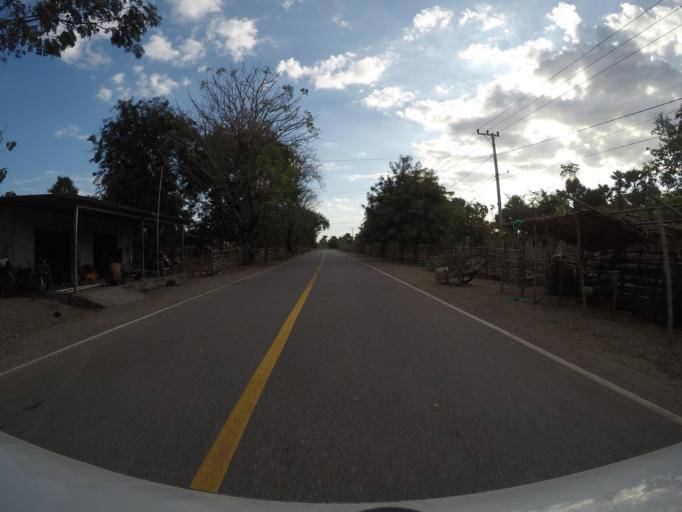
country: TL
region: Bobonaro
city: Maliana
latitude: -8.8817
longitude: 125.0303
